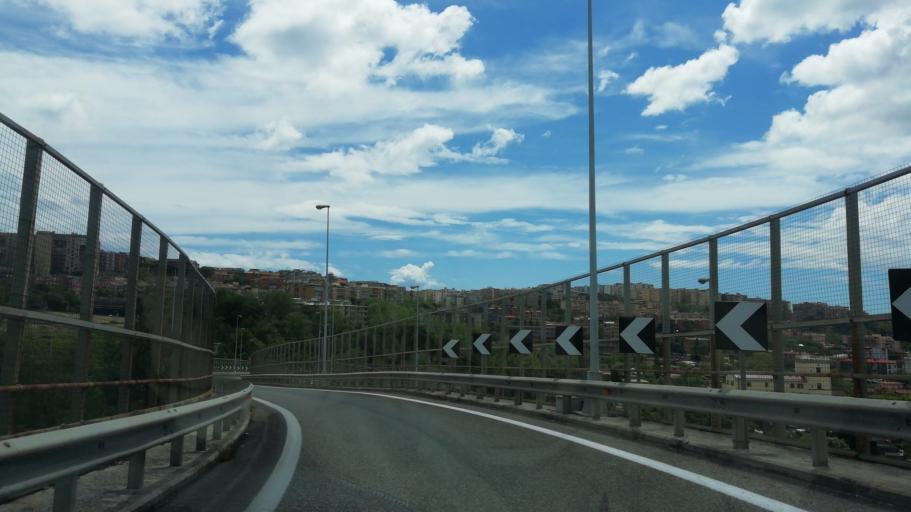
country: IT
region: Campania
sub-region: Provincia di Napoli
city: Napoli
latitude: 40.8469
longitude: 14.2115
